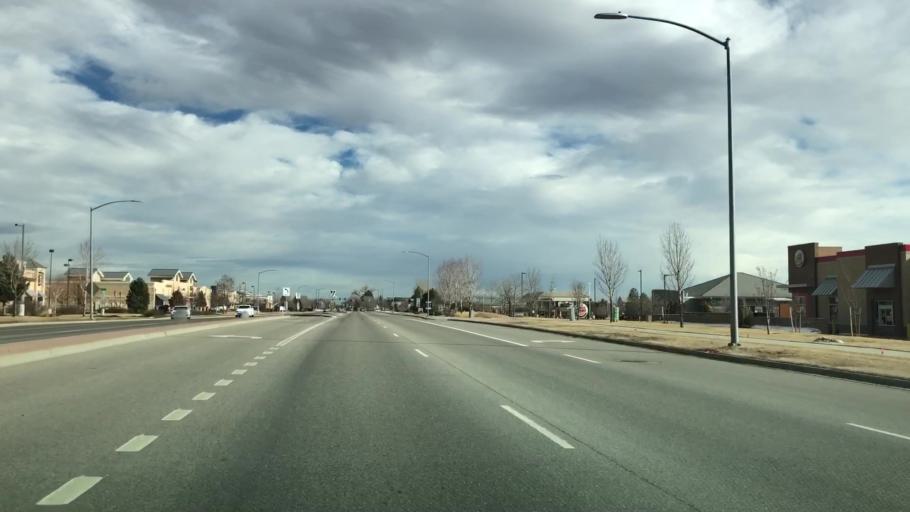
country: US
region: Colorado
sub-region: Weld County
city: Windsor
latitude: 40.4795
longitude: -104.9320
